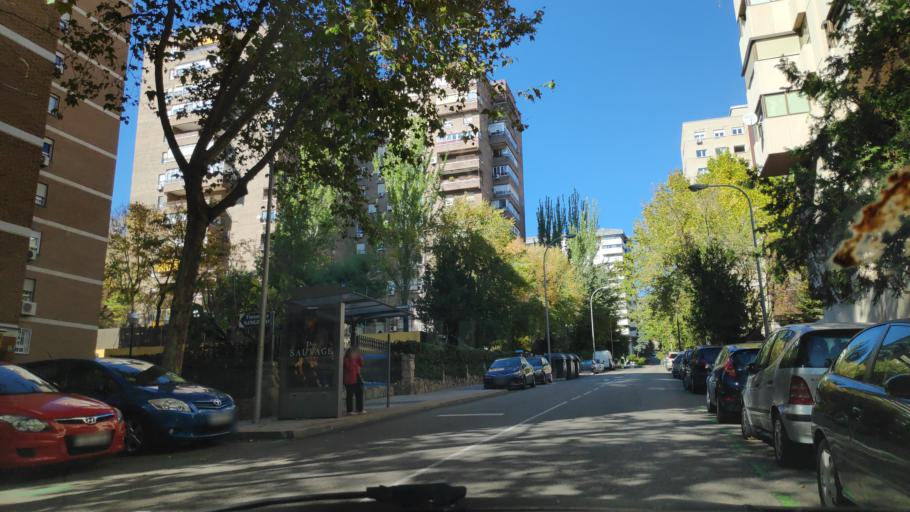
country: ES
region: Madrid
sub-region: Provincia de Madrid
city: Tetuan de las Victorias
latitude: 40.4843
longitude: -3.7029
